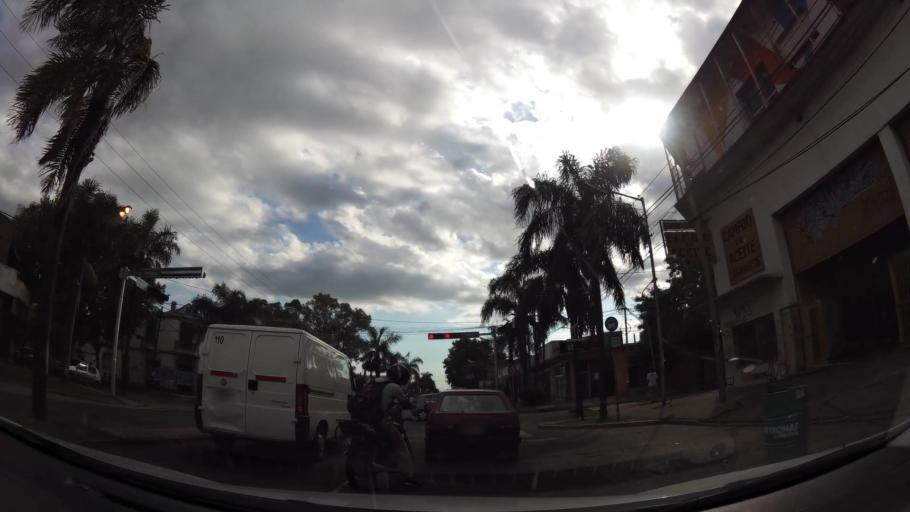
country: AR
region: Buenos Aires
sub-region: Partido de Tigre
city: Tigre
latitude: -34.4690
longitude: -58.6507
